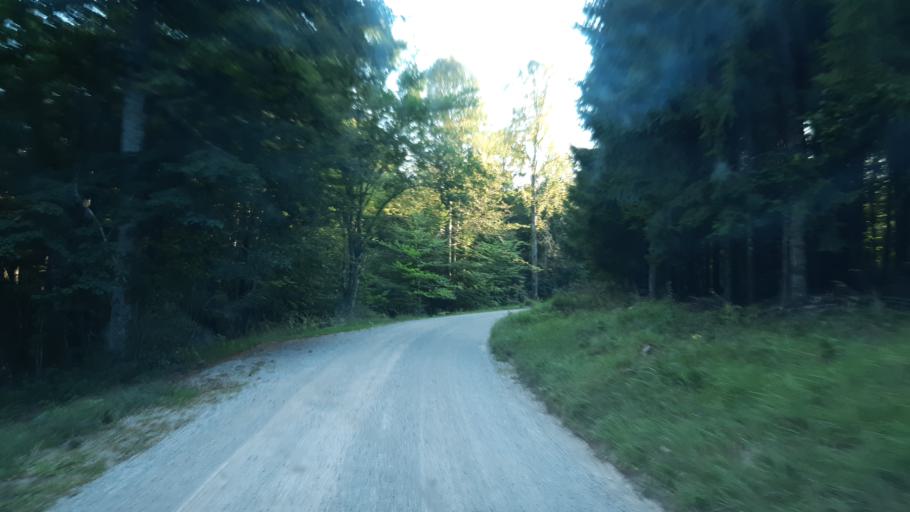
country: SI
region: Kocevje
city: Kocevje
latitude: 45.6661
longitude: 14.9535
